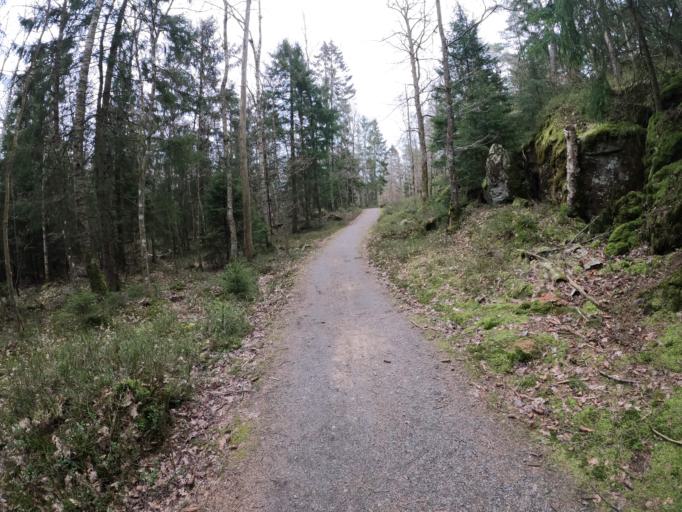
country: SE
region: Vaestra Goetaland
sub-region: Harryda Kommun
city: Molnlycke
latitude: 57.6225
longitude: 12.1069
